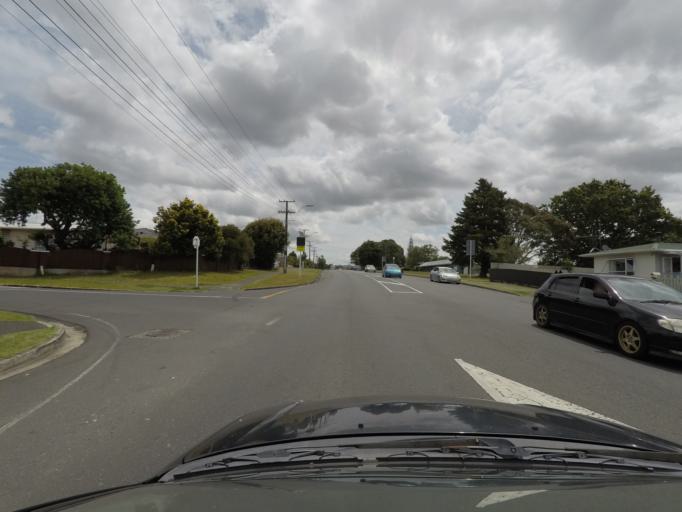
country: NZ
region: Northland
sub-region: Whangarei
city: Whangarei
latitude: -35.6842
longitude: 174.3317
